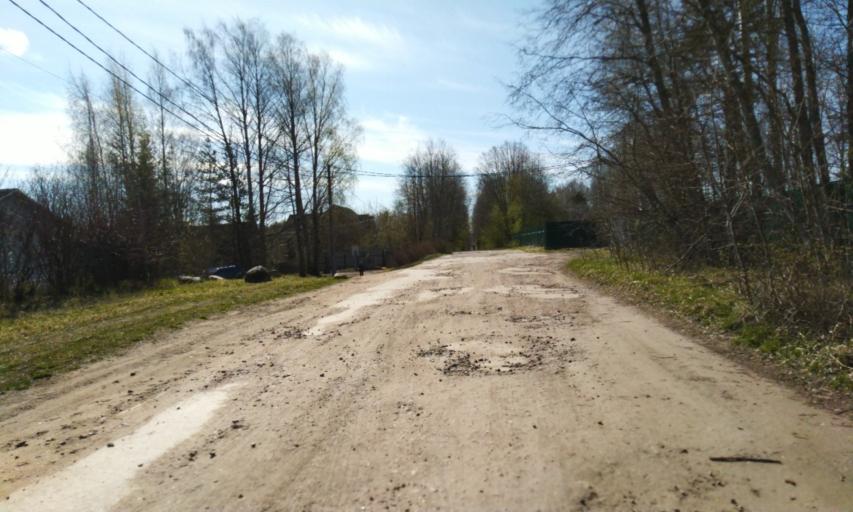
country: RU
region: Leningrad
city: Garbolovo
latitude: 60.3897
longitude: 30.4810
